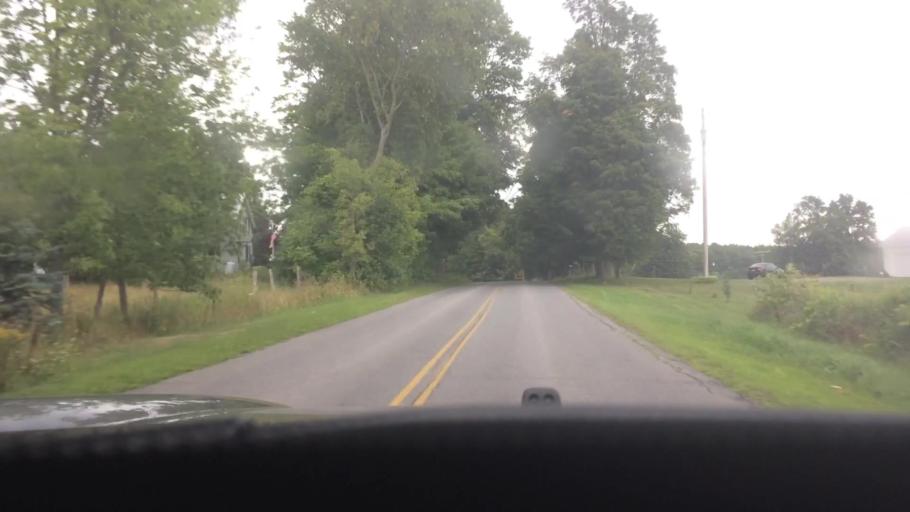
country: US
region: New York
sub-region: St. Lawrence County
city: Canton
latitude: 44.5567
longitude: -75.1260
